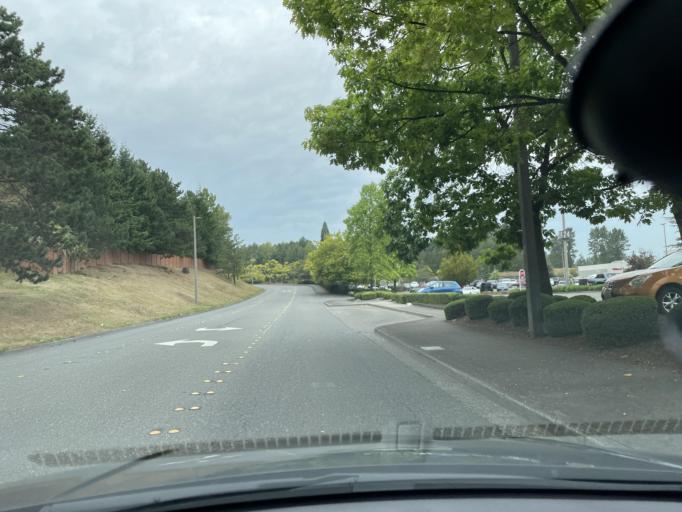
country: US
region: Washington
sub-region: Whatcom County
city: Bellingham
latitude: 48.7851
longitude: -122.4941
